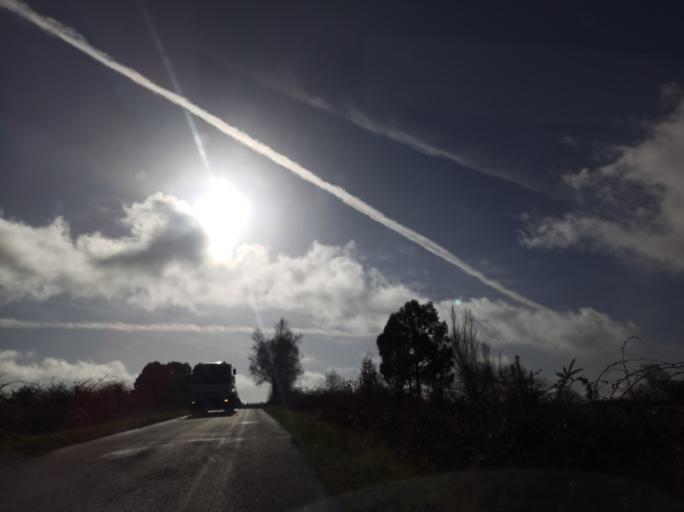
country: ES
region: Galicia
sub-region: Provincia da Coruna
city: Sobrado
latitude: 43.0879
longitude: -7.9673
